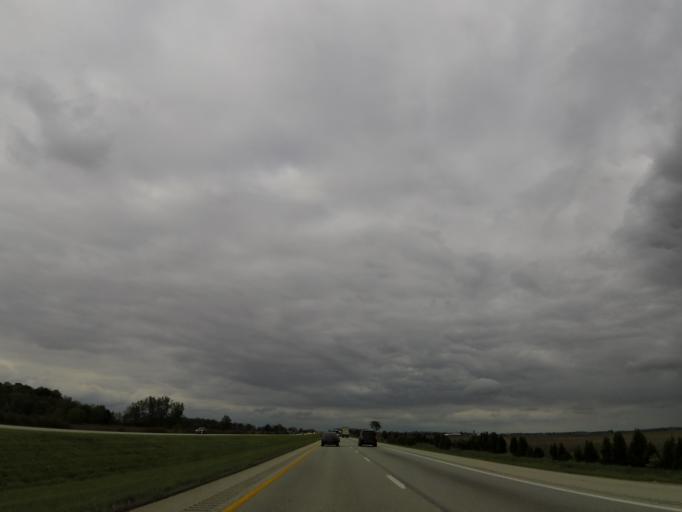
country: US
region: Ohio
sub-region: Clinton County
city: Wilmington
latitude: 39.5295
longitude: -83.8094
